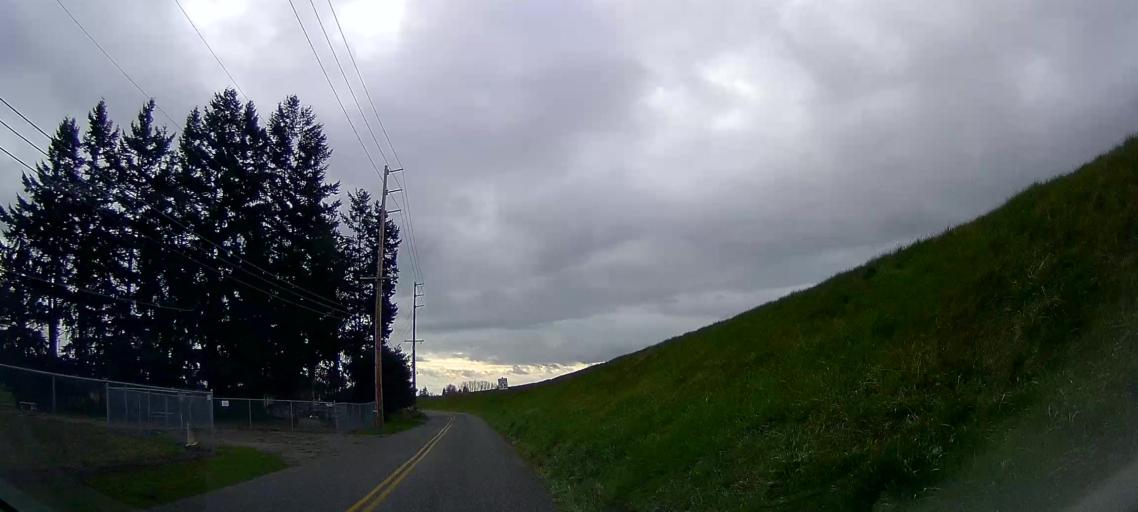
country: US
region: Washington
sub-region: Skagit County
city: Mount Vernon
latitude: 48.4407
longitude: -122.3725
